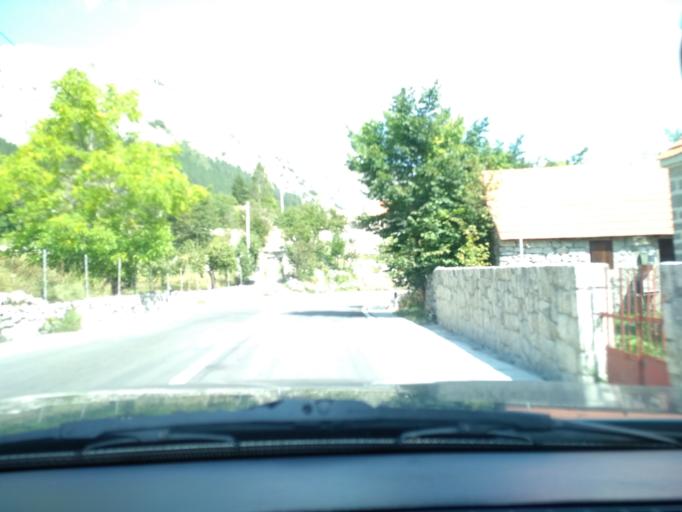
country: ME
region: Kotor
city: Kotor
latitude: 42.4323
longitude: 18.8086
